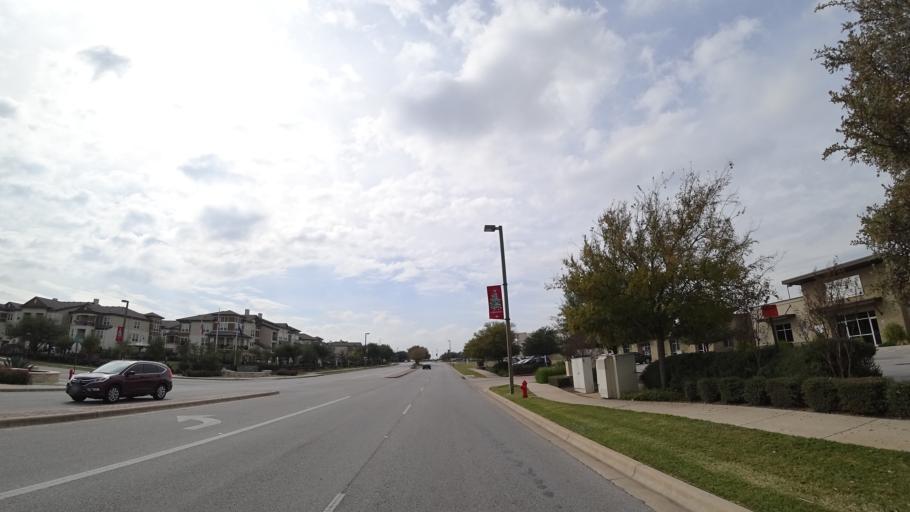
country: US
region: Texas
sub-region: Williamson County
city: Round Rock
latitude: 30.4838
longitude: -97.6910
